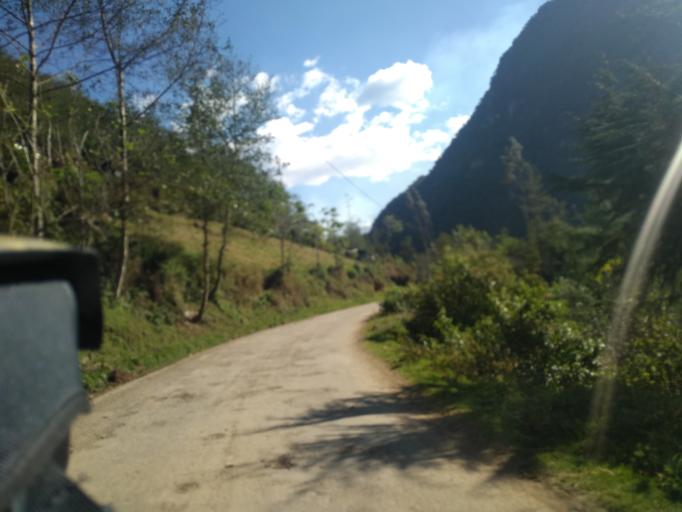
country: PE
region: Amazonas
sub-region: Provincia de Chachapoyas
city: Montevideo
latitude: -6.7195
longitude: -77.8224
